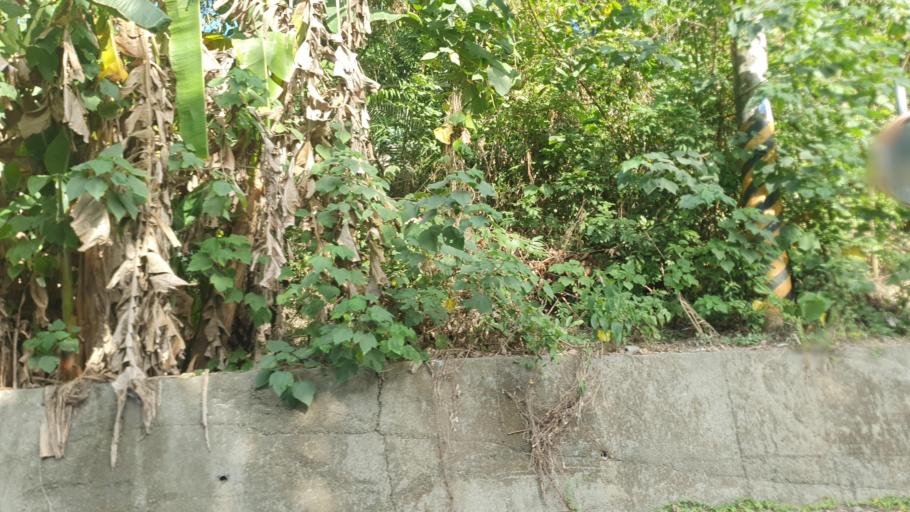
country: TW
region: Taiwan
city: Yujing
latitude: 23.0453
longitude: 120.3981
